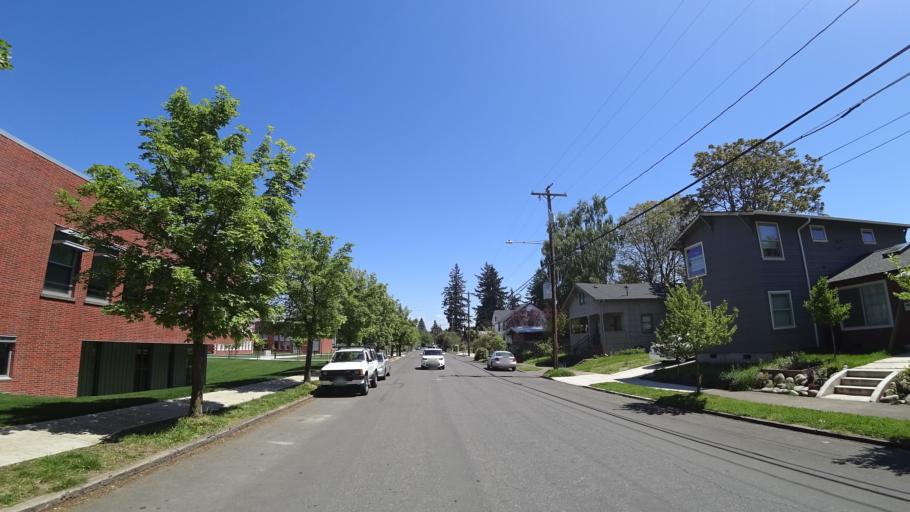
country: US
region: Oregon
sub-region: Multnomah County
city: Lents
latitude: 45.5014
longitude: -122.6078
